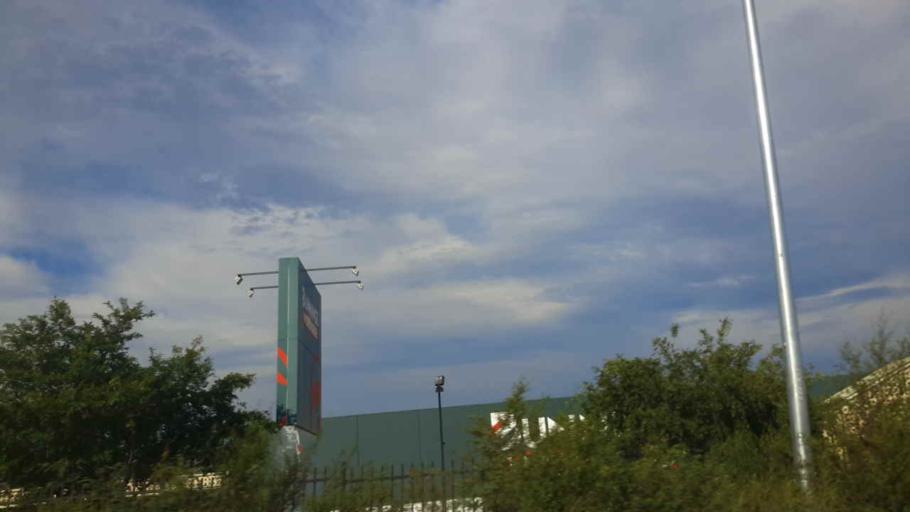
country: AU
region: New South Wales
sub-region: Camden
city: Narellan
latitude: -34.0342
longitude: 150.7309
